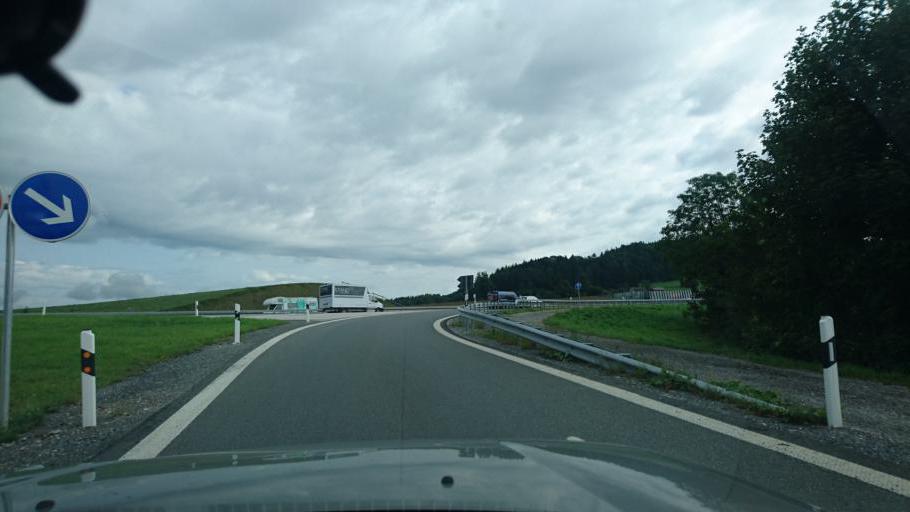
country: DE
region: Bavaria
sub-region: Upper Bavaria
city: Bergen
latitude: 47.8275
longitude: 12.5985
